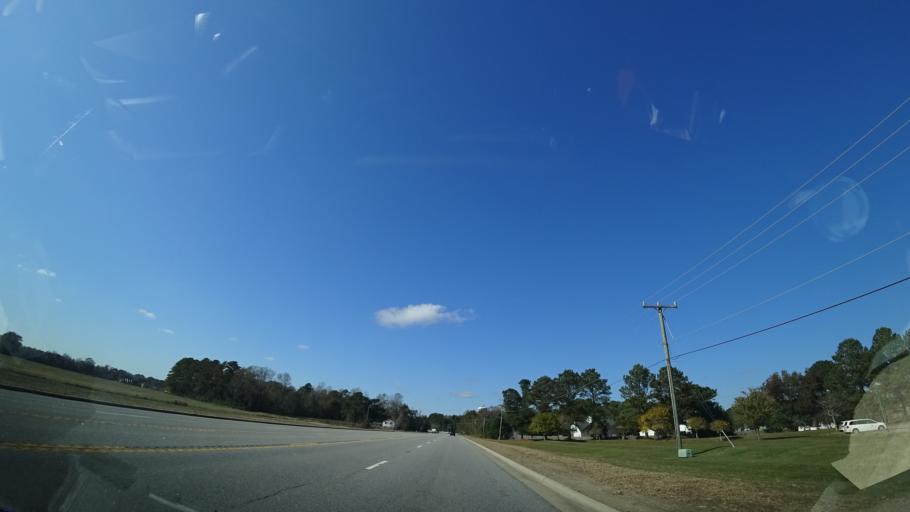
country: US
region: North Carolina
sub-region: Currituck County
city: Currituck
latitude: 36.4527
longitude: -76.0240
